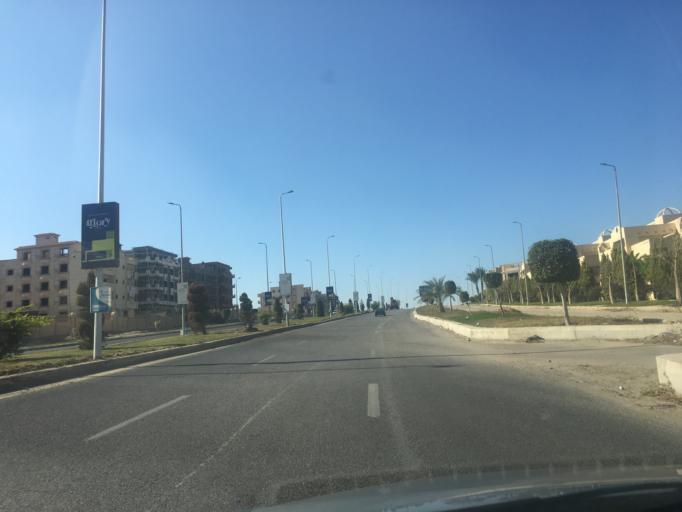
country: EG
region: Al Jizah
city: Awsim
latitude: 30.0198
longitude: 30.9864
